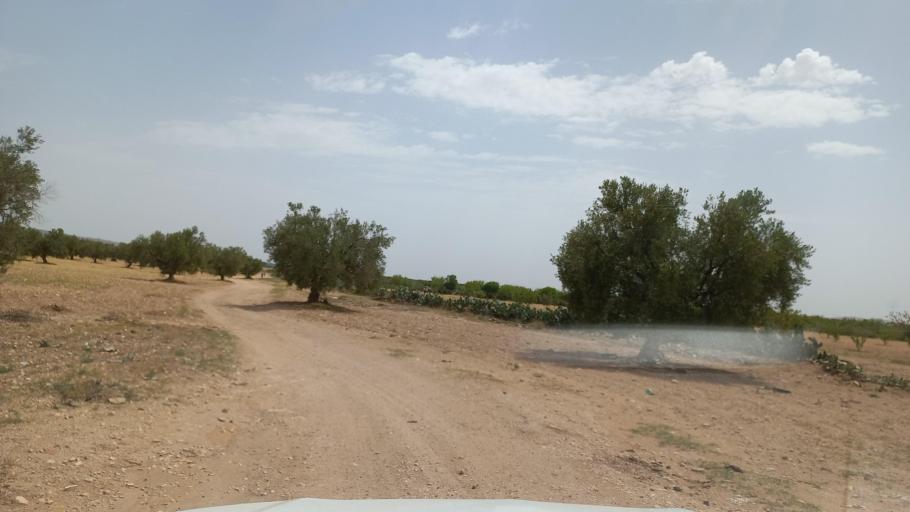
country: TN
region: Al Qasrayn
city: Kasserine
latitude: 35.2908
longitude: 9.0208
